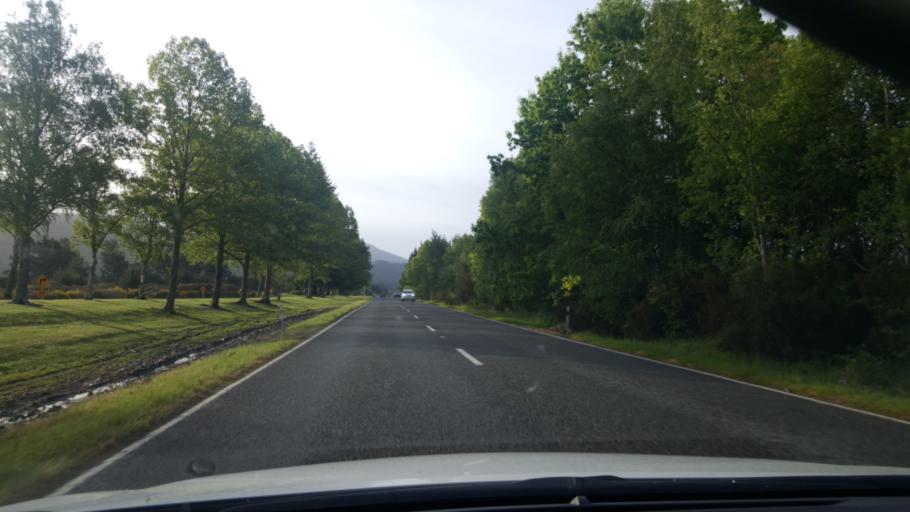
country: NZ
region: Waikato
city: Turangi
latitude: -38.9922
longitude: 175.7964
